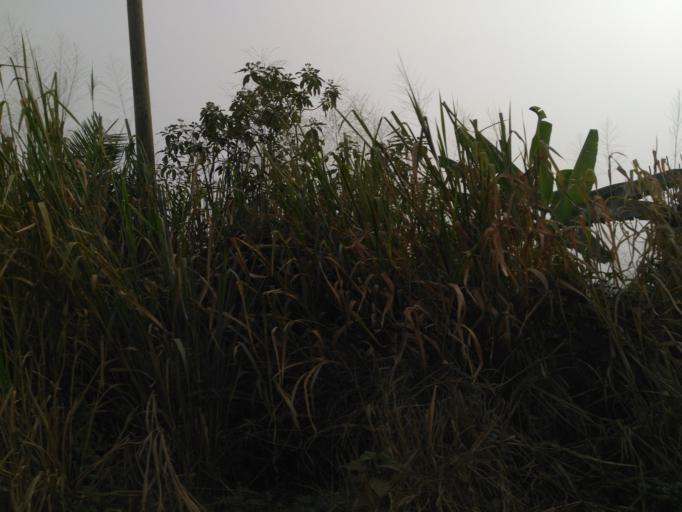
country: GH
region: Ashanti
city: Kumasi
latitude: 6.6542
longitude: -1.6252
